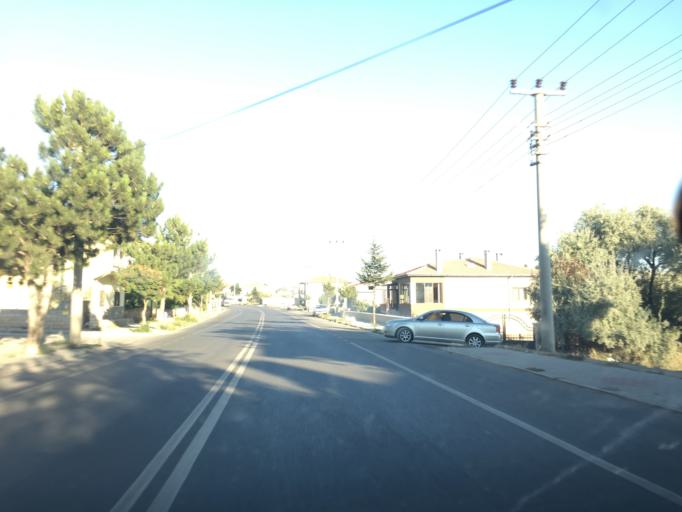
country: TR
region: Nevsehir
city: Avanos
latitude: 38.7194
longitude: 34.8377
